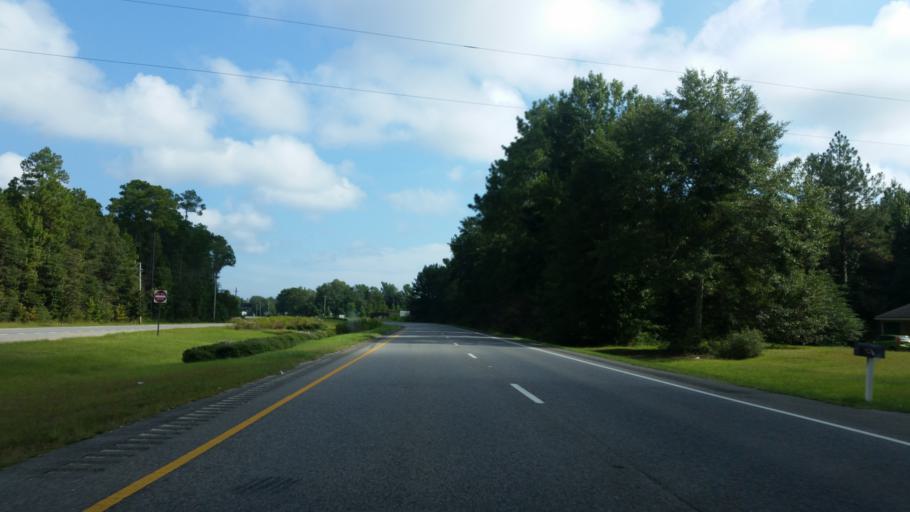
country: US
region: Alabama
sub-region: Baldwin County
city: Bay Minette
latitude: 30.9371
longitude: -87.7674
